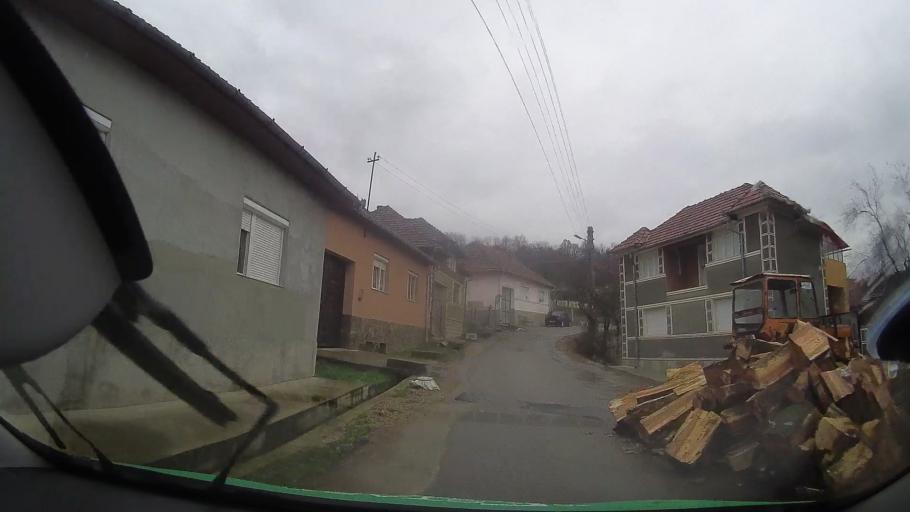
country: RO
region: Bihor
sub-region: Comuna Uileacu de Beius
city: Forau
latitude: 46.7177
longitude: 22.2298
